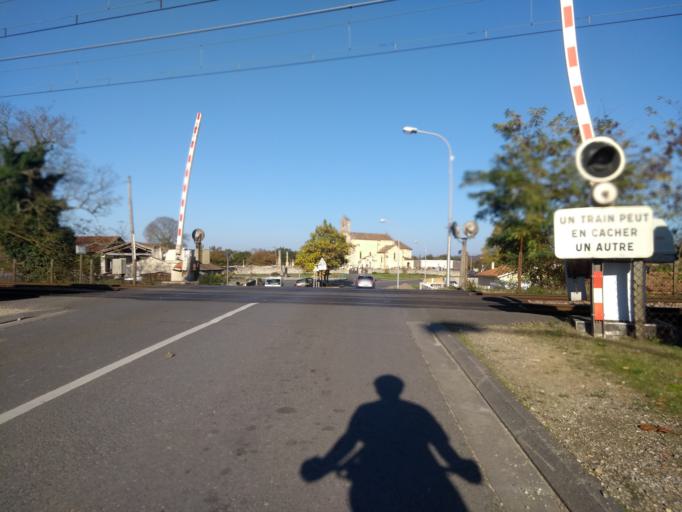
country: FR
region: Aquitaine
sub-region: Departement de la Gironde
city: Martillac
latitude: 44.7194
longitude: -0.5092
